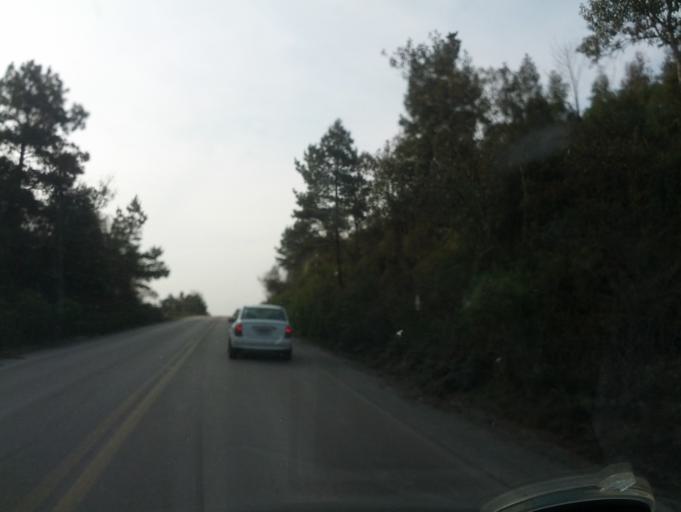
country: BR
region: Santa Catarina
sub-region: Otacilio Costa
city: Otacilio Costa
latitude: -27.4516
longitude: -50.1231
